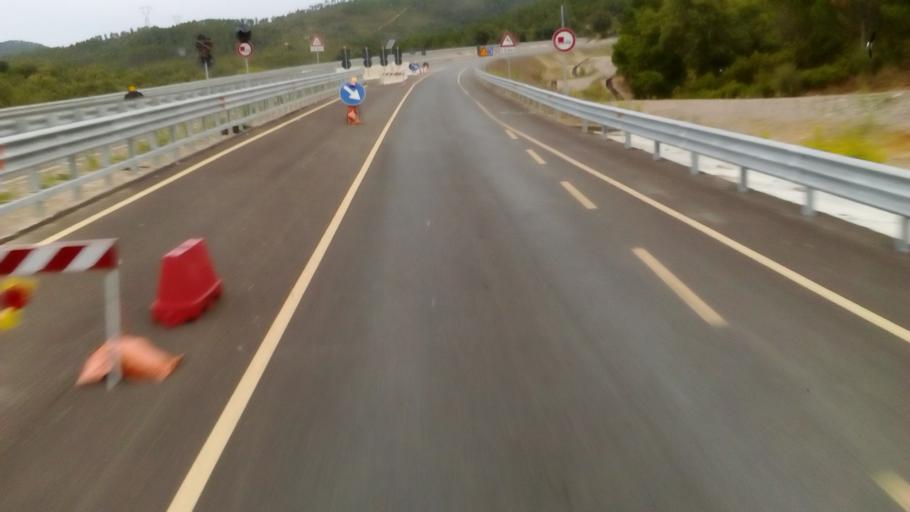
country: IT
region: Tuscany
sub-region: Provincia di Grosseto
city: Civitella Marittima
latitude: 43.0314
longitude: 11.2768
